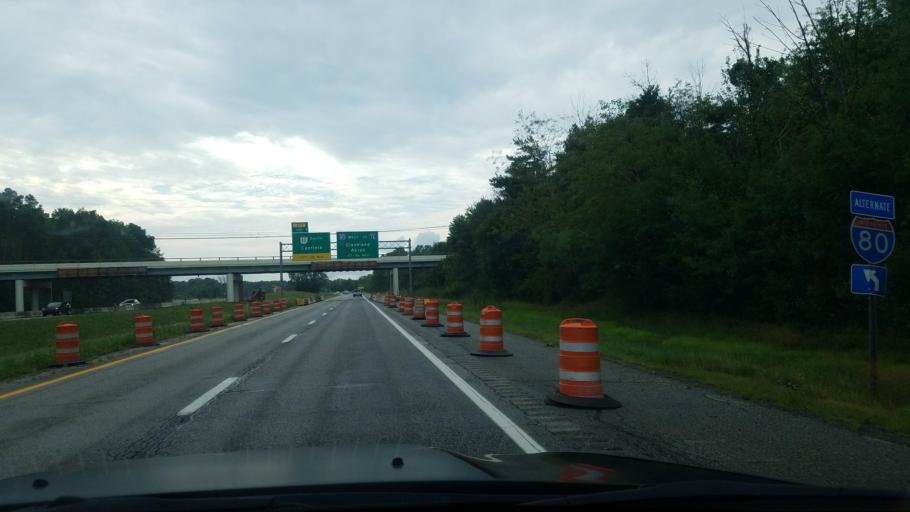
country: US
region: Ohio
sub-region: Trumbull County
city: Mineral Ridge
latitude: 41.1265
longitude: -80.7358
